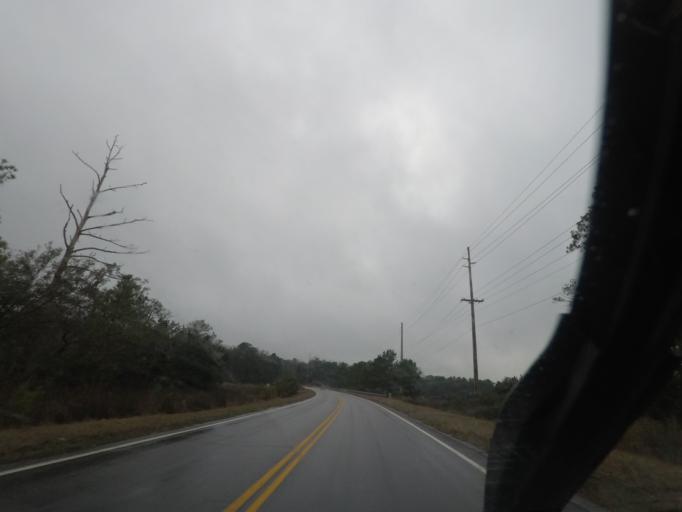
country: US
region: South Carolina
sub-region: Charleston County
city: Meggett
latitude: 32.6839
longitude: -80.3511
